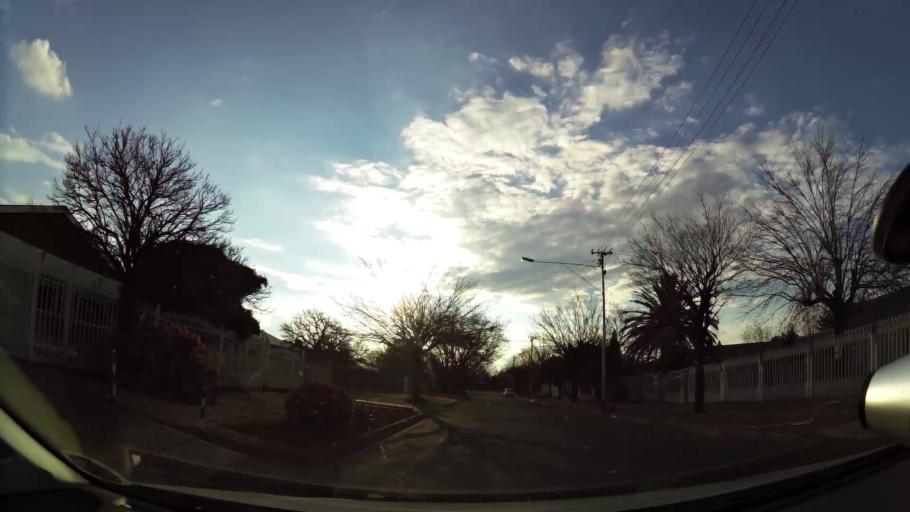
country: ZA
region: Orange Free State
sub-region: Mangaung Metropolitan Municipality
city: Bloemfontein
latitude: -29.1399
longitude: 26.1963
